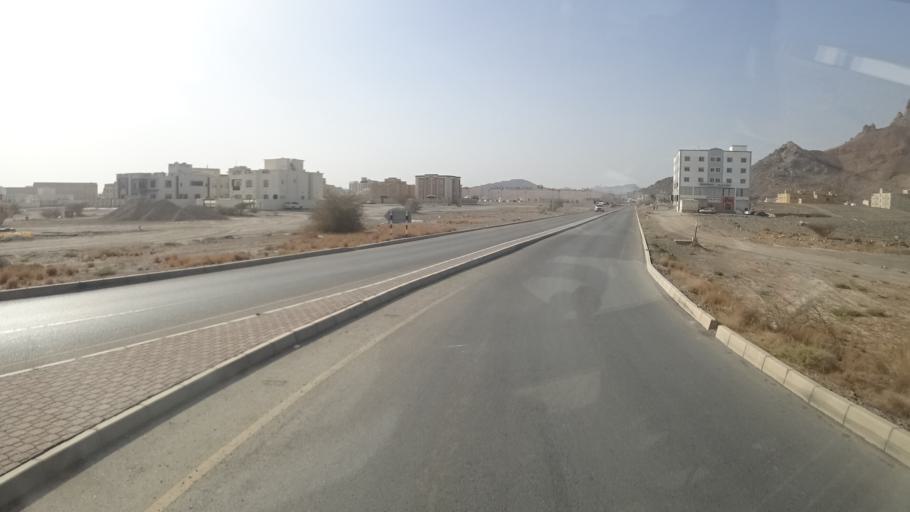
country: OM
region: Muhafazat ad Dakhiliyah
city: Nizwa
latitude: 22.8734
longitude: 57.5423
